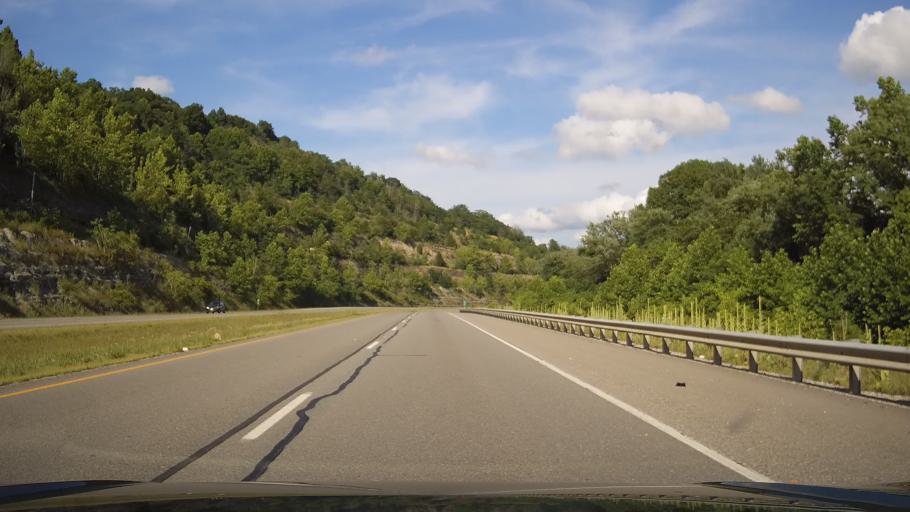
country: US
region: Kentucky
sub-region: Lawrence County
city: Louisa
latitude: 38.1713
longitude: -82.6406
